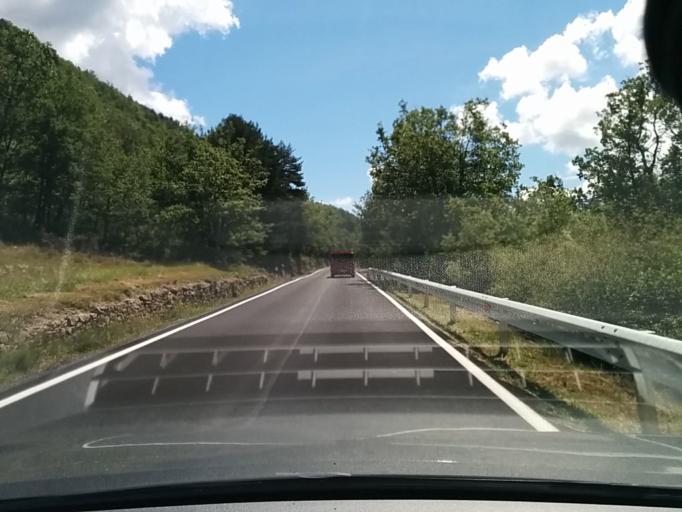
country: ES
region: Aragon
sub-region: Provincia de Huesca
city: Fiscal
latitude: 42.4897
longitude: -0.0964
